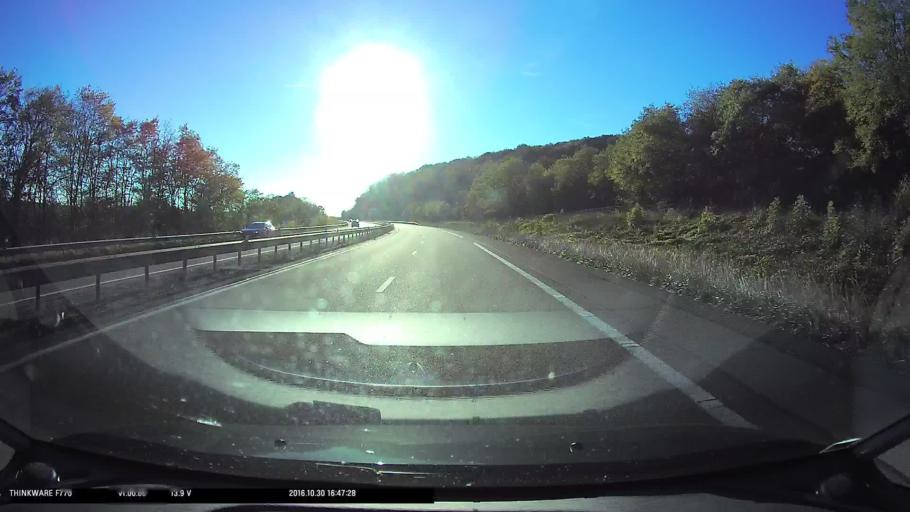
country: FR
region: Franche-Comte
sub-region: Departement du Doubs
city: Chatillon-le-Duc
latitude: 47.2858
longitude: 6.0048
